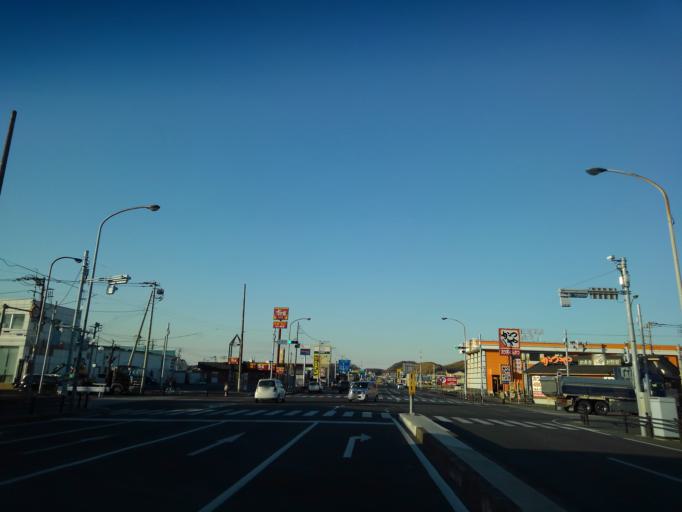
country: JP
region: Chiba
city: Kimitsu
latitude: 35.3181
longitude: 139.9266
